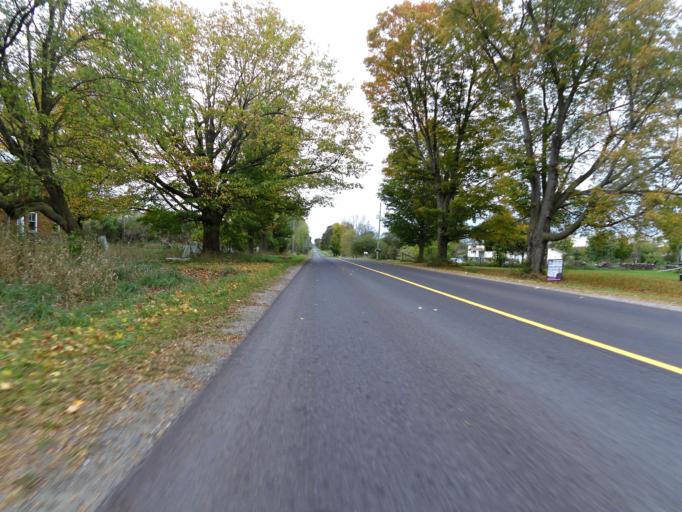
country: US
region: New York
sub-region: Jefferson County
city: Alexandria Bay
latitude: 44.5835
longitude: -76.0358
